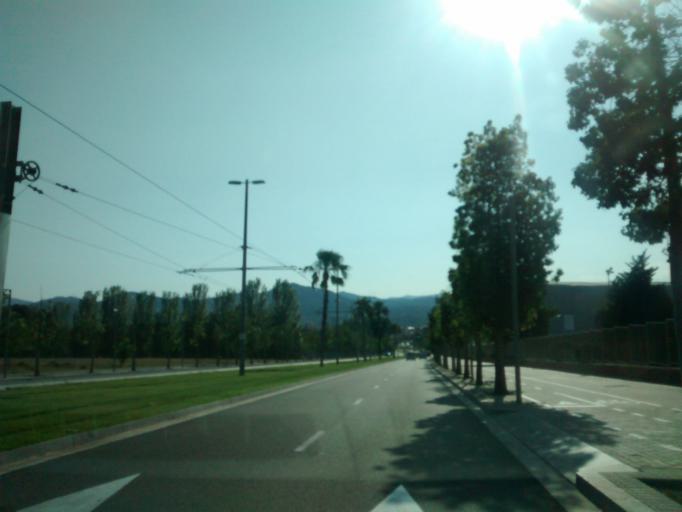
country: ES
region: Catalonia
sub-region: Provincia de Barcelona
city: Sant Feliu de Llobregat
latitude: 41.3799
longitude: 2.0600
